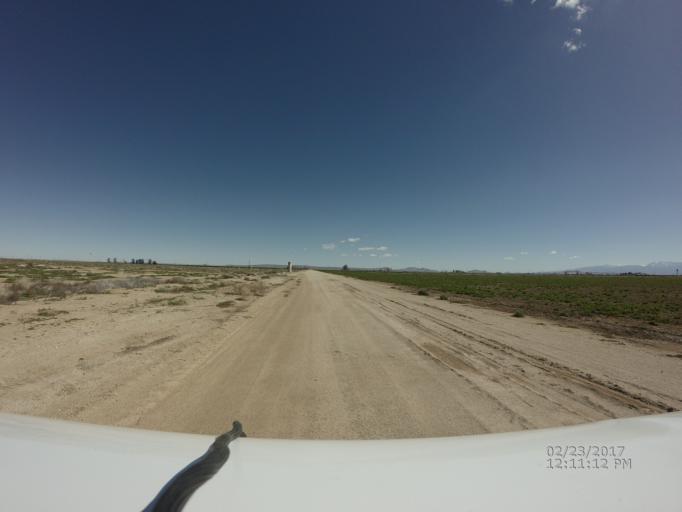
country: US
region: California
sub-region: Los Angeles County
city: Lancaster
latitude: 34.7414
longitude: -118.0128
